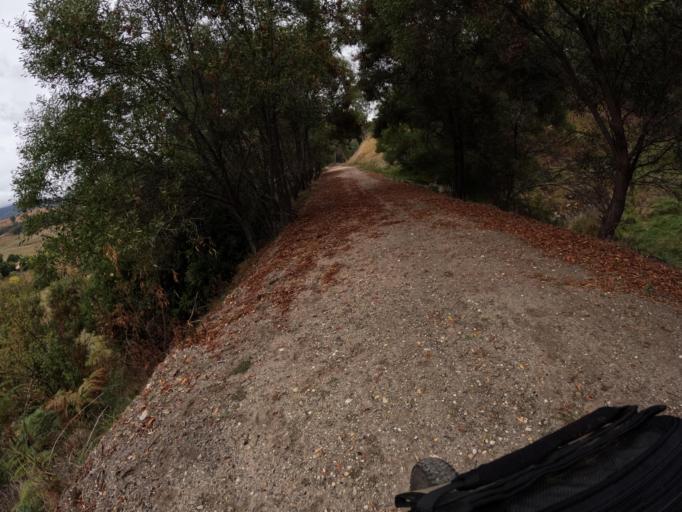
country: AU
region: New South Wales
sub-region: Greater Hume Shire
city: Holbrook
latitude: -36.1766
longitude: 147.3826
